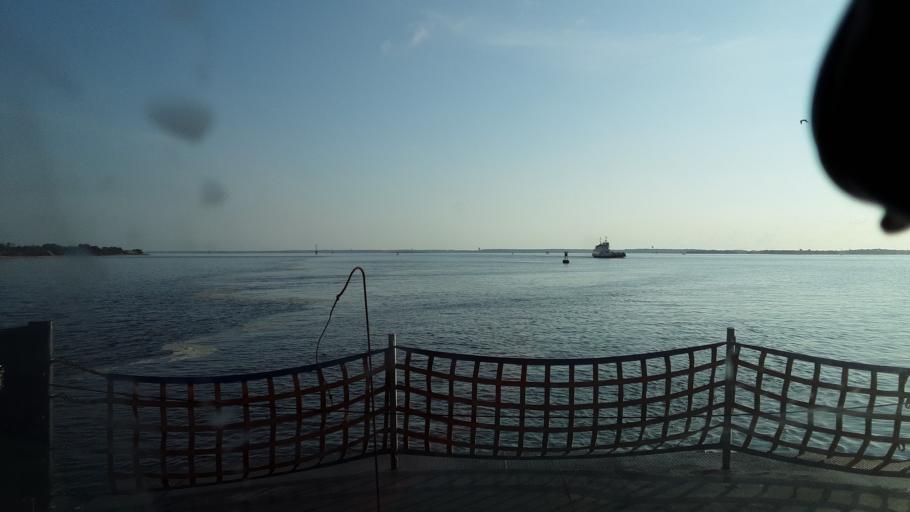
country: US
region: North Carolina
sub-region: Brunswick County
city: Southport
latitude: 33.9530
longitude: -77.9616
